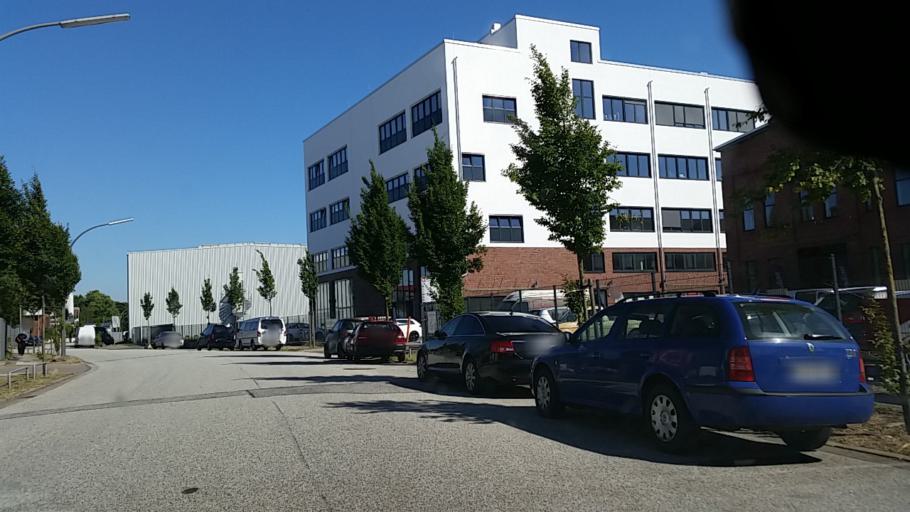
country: DE
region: Hamburg
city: Rothenburgsort
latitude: 53.5464
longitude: 10.0454
